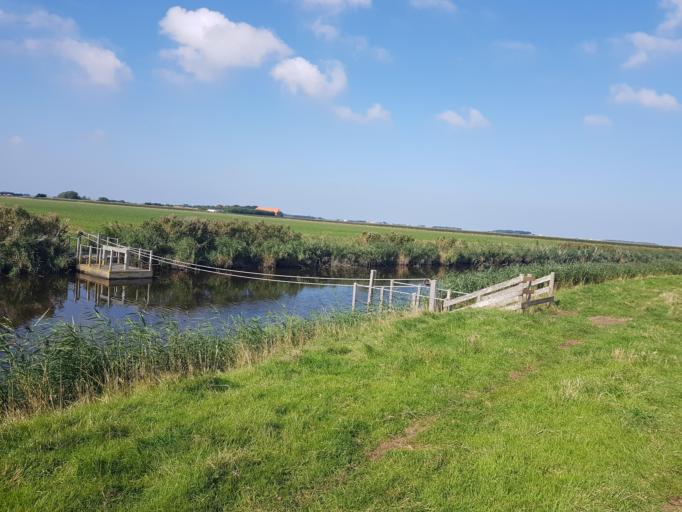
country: NL
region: North Holland
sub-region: Gemeente Texel
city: Den Burg
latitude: 53.1061
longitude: 4.8601
